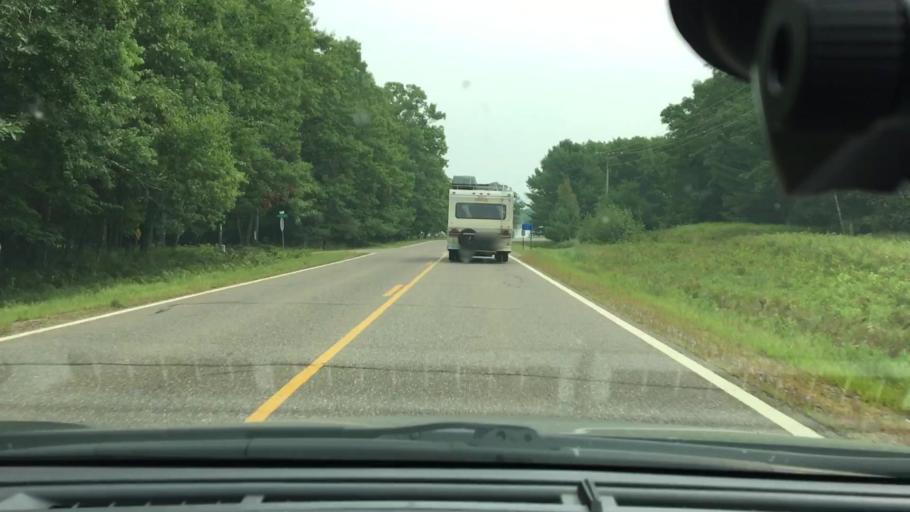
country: US
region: Minnesota
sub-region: Aitkin County
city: Aitkin
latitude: 46.4045
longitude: -93.7814
